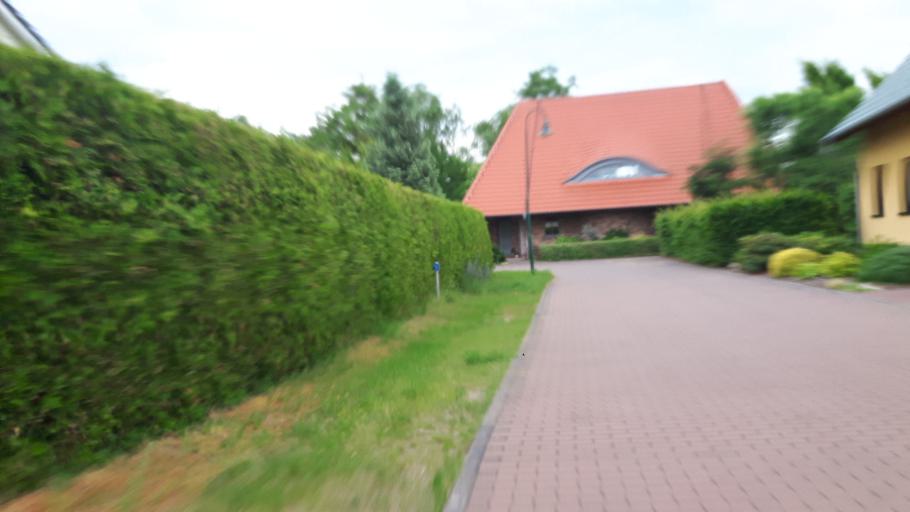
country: DE
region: Brandenburg
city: Schwedt (Oder)
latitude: 53.0485
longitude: 14.2749
